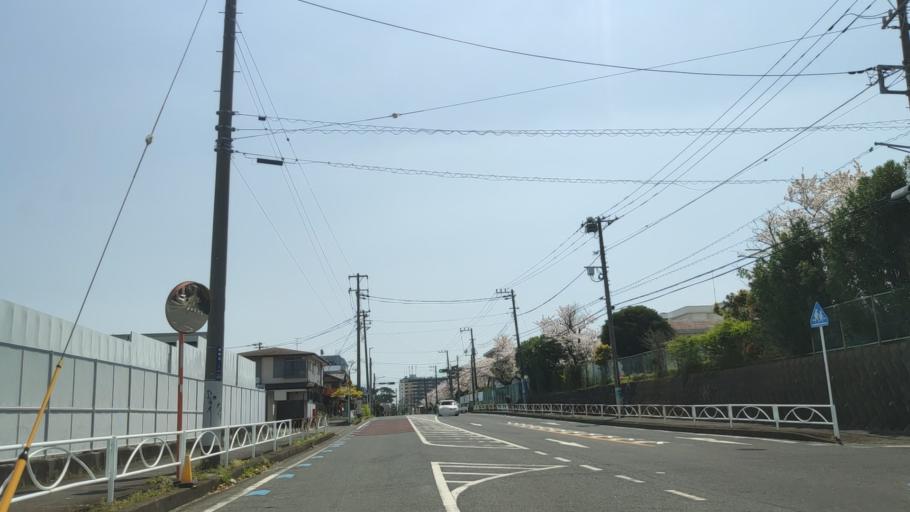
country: JP
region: Kanagawa
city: Hiratsuka
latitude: 35.3236
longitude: 139.3381
